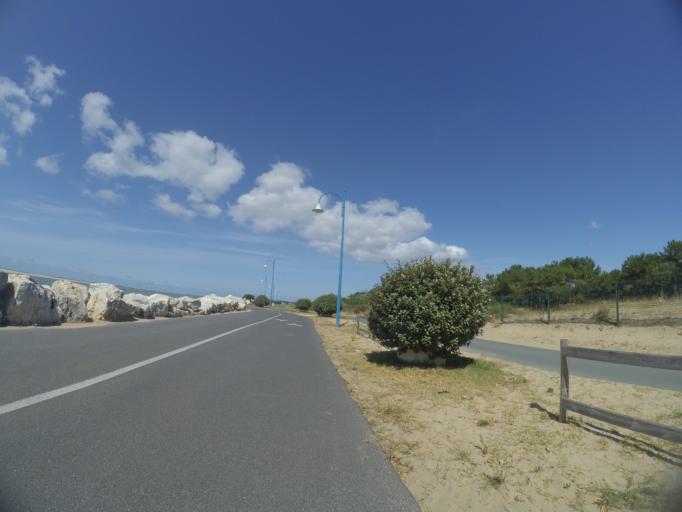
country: FR
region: Poitou-Charentes
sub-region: Departement de la Charente-Maritime
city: Les Mathes
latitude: 45.6778
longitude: -1.1710
